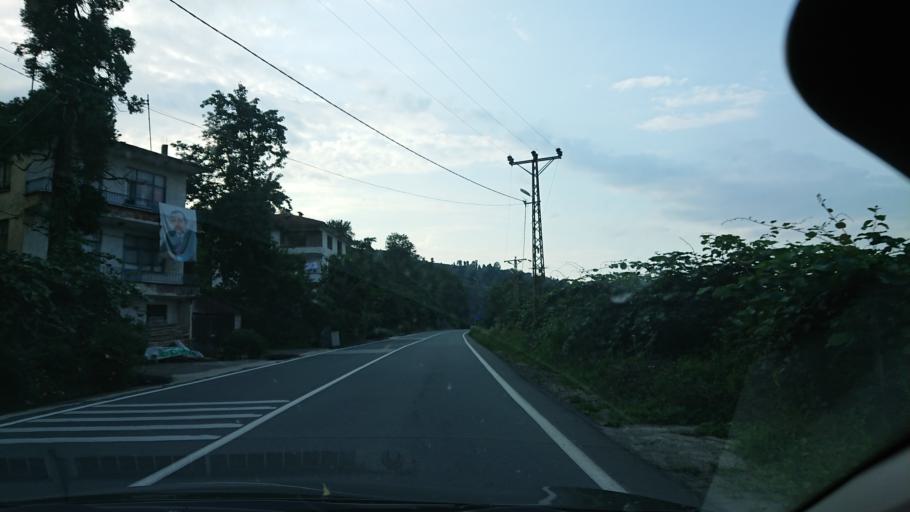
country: TR
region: Rize
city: Cayeli
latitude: 41.0666
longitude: 40.7142
